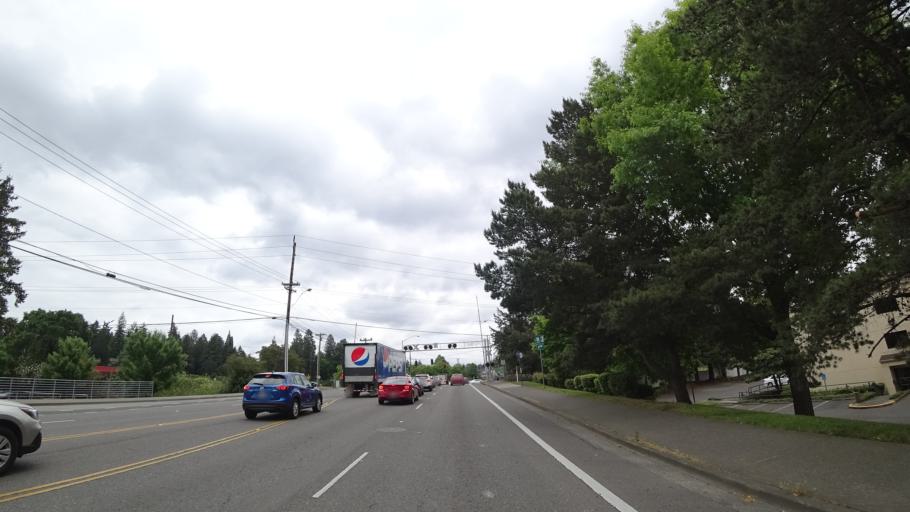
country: US
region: Oregon
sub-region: Washington County
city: Garden Home-Whitford
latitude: 45.4589
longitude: -122.7878
